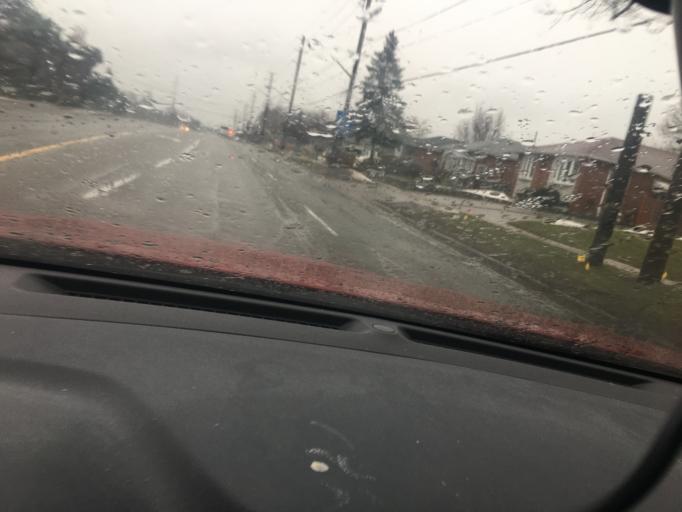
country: CA
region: Ontario
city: Scarborough
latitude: 43.7581
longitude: -79.2568
